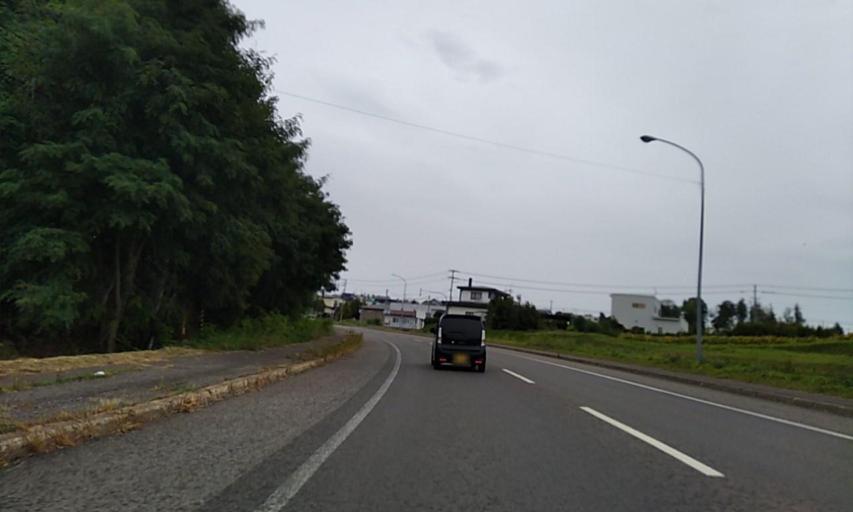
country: JP
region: Hokkaido
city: Bihoro
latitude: 43.9128
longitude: 144.1808
